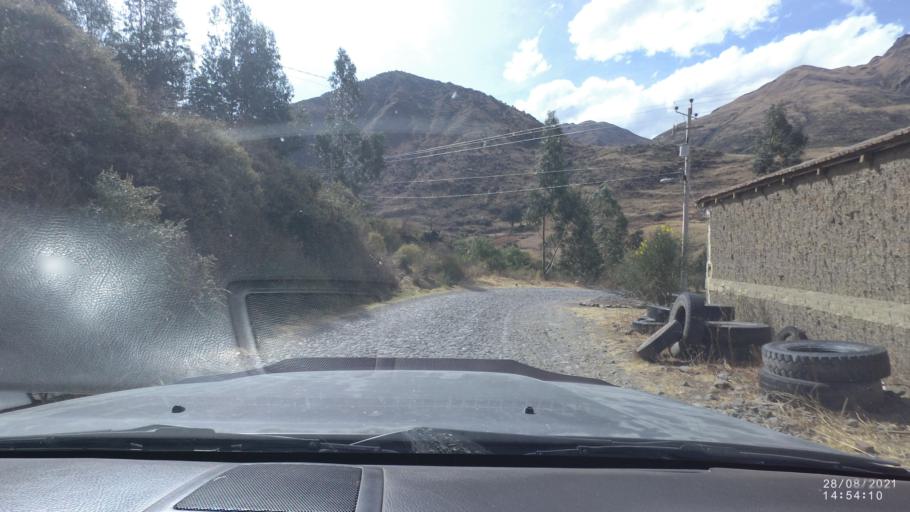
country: BO
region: Cochabamba
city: Sipe Sipe
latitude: -17.2848
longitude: -66.3066
